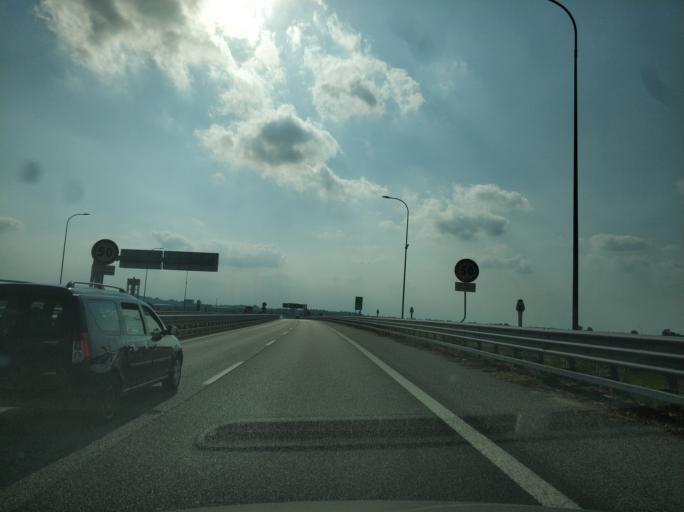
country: IT
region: Piedmont
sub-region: Provincia di Cuneo
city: Roreto
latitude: 44.6649
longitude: 7.8043
